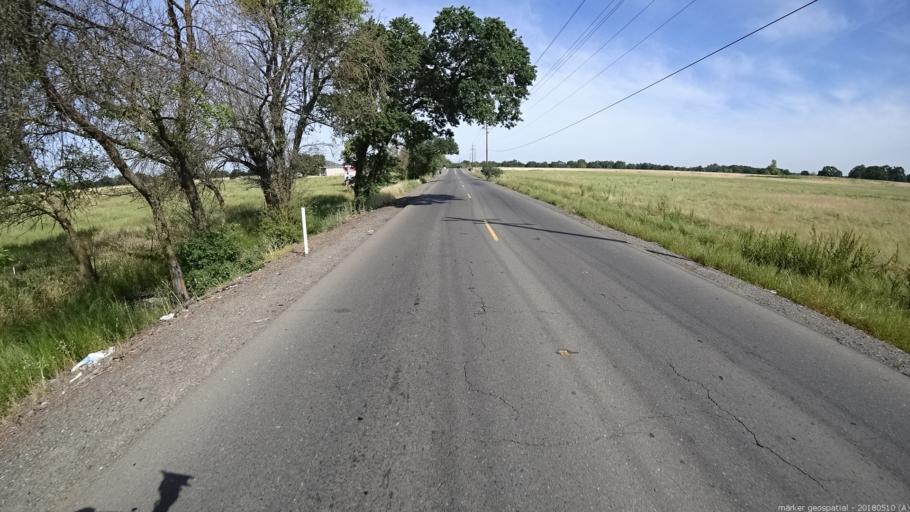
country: US
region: California
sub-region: Sacramento County
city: Rio Linda
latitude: 38.6649
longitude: -121.4496
